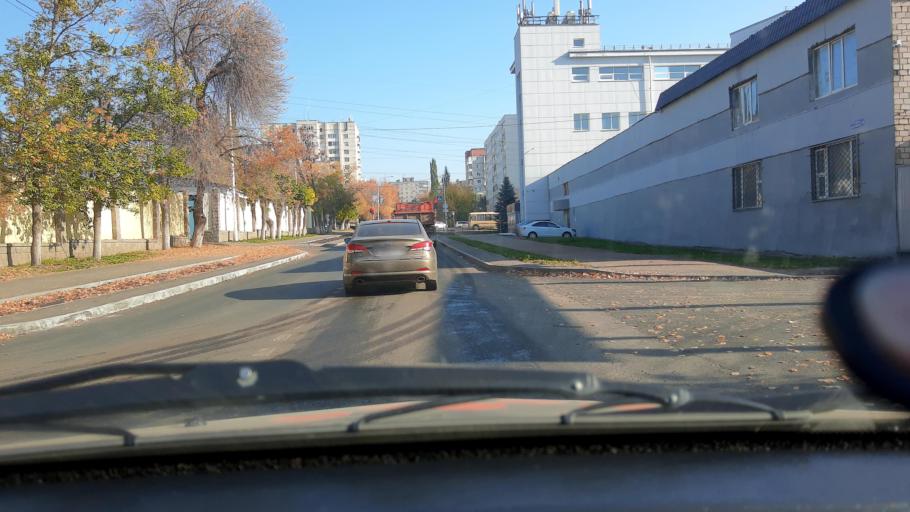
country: RU
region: Bashkortostan
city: Ufa
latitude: 54.7547
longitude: 56.0159
